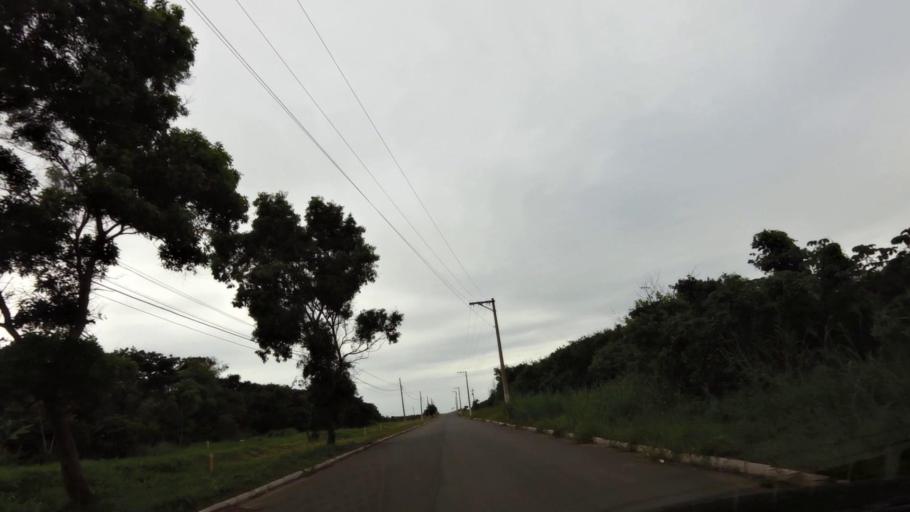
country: BR
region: Espirito Santo
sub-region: Piuma
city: Piuma
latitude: -20.8005
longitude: -40.5863
